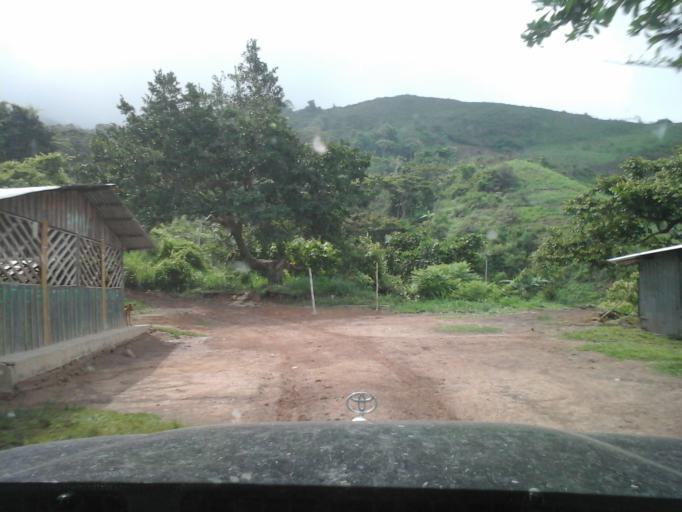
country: CO
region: Cesar
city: Agustin Codazzi
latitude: 9.9540
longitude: -73.0647
